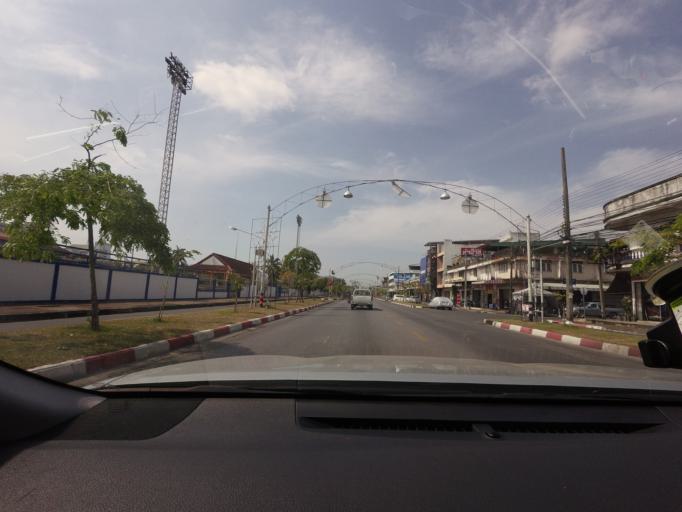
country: TH
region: Yala
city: Yala
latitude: 6.5527
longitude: 101.2878
